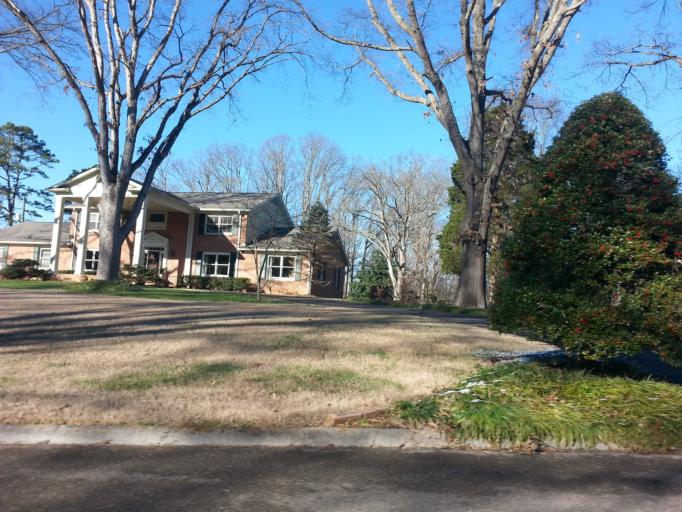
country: US
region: Tennessee
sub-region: Blount County
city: Louisville
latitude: 35.9124
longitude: -84.0131
